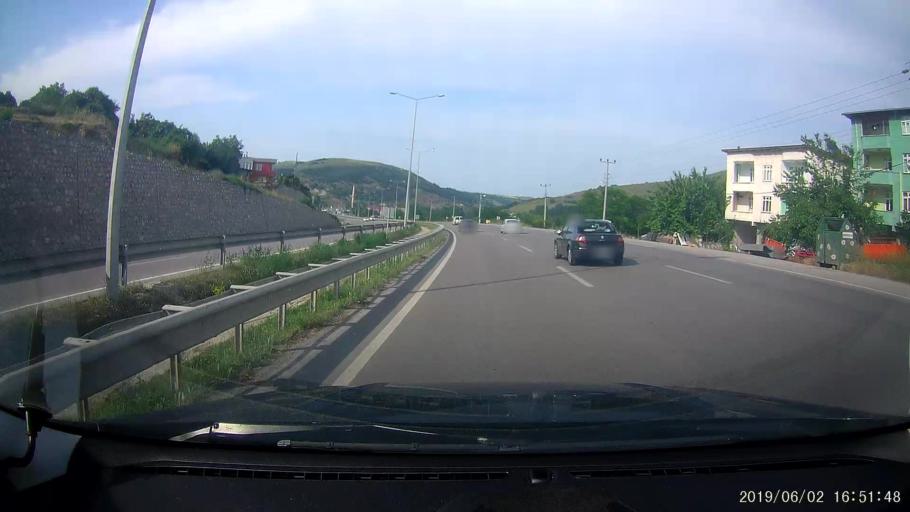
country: TR
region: Samsun
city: Samsun
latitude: 41.2785
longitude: 36.1886
